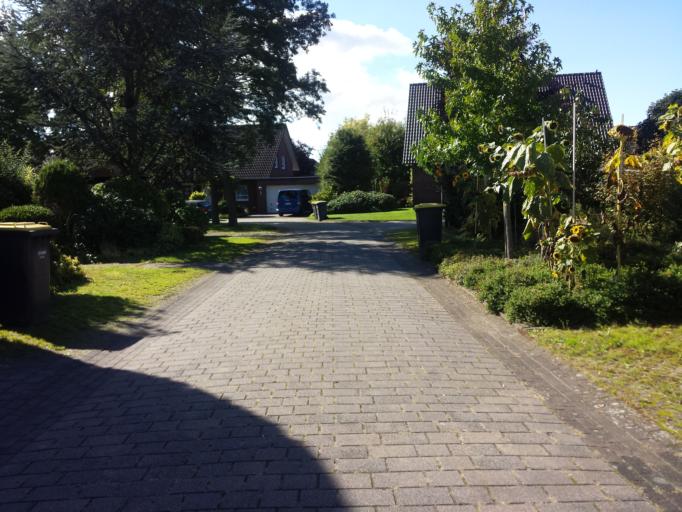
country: DE
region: North Rhine-Westphalia
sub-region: Regierungsbezirk Detmold
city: Langenberg
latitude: 51.7657
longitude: 8.3159
